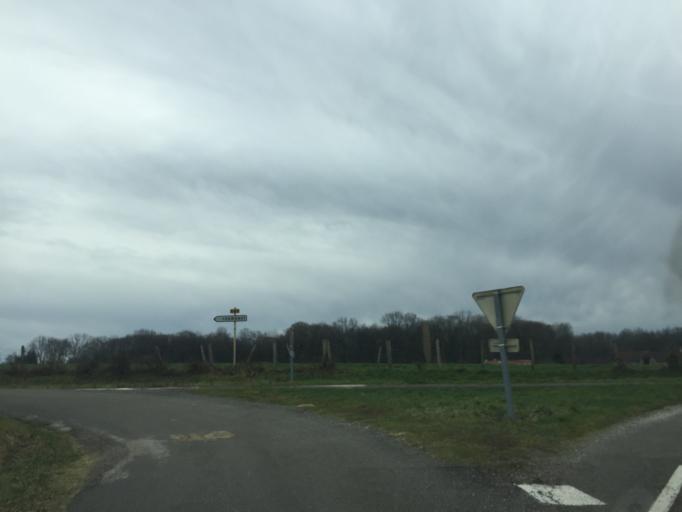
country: FR
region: Franche-Comte
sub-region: Departement du Jura
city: Mont-sous-Vaudrey
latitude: 46.8654
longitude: 5.5260
